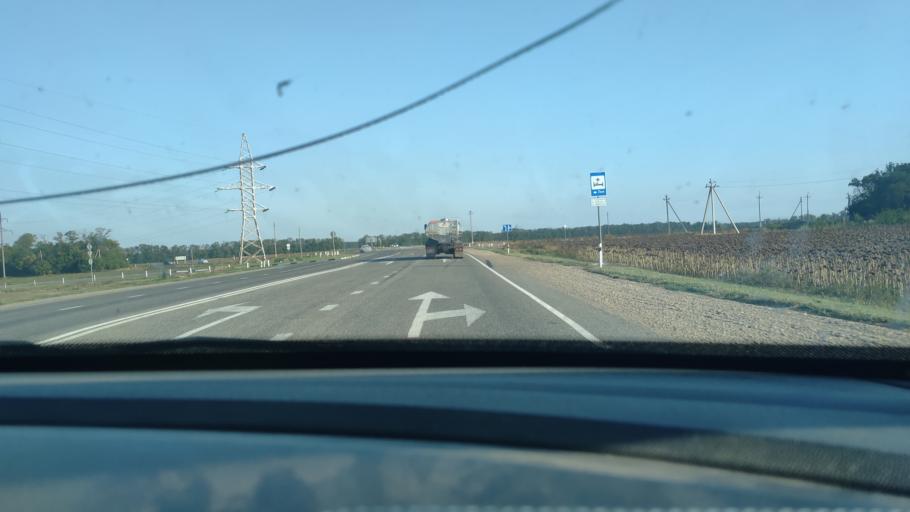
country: RU
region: Krasnodarskiy
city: Starominskaya
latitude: 46.5035
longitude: 39.0381
